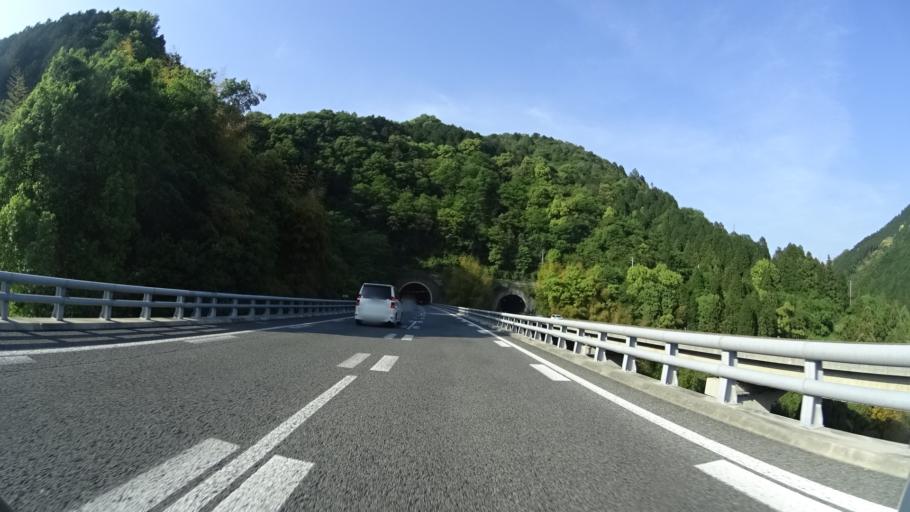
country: JP
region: Ehime
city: Saijo
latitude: 33.8904
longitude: 133.1967
